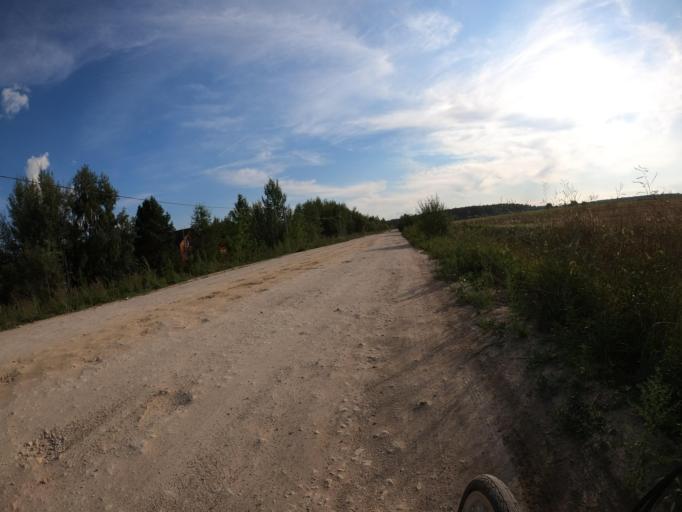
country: RU
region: Moskovskaya
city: Meshcherino
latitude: 55.1429
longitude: 38.4383
